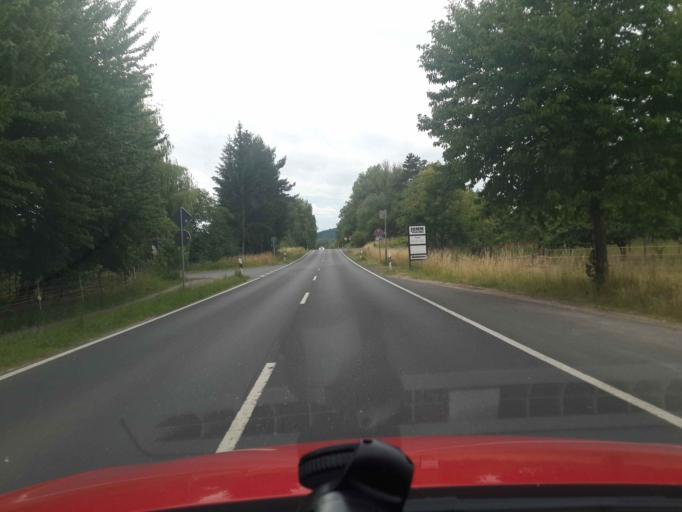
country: DE
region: Bavaria
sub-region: Regierungsbezirk Unterfranken
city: Sulzbach am Main
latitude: 49.8932
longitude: 9.1460
